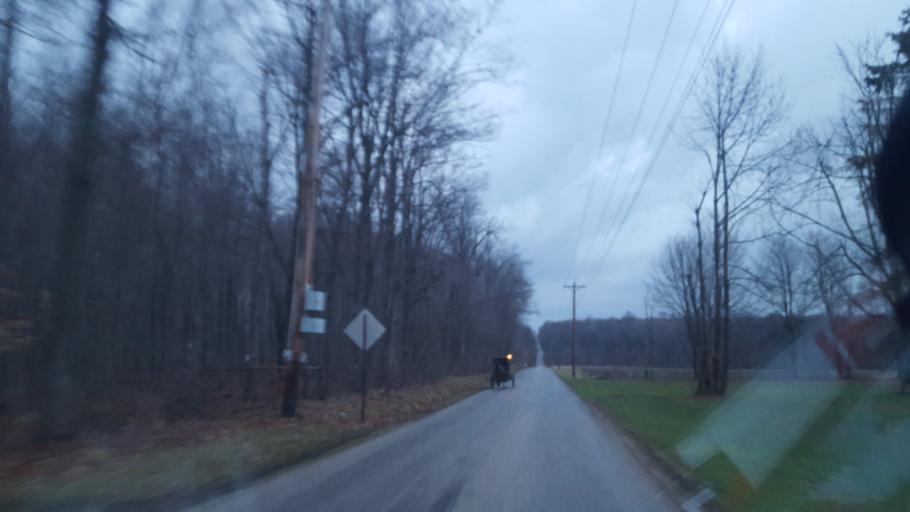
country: US
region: Ohio
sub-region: Richland County
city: Lexington
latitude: 40.5879
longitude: -82.6051
